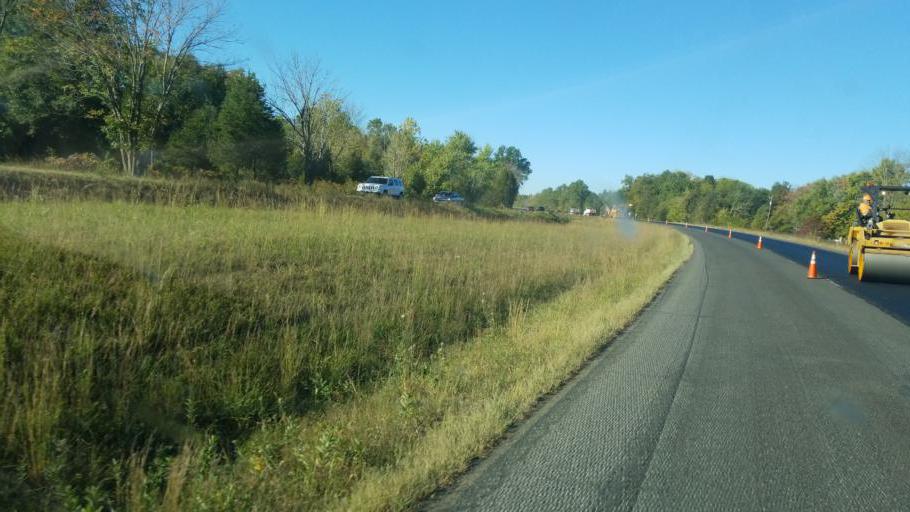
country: US
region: Virginia
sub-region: Fauquier County
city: Bealeton
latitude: 38.5236
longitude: -77.8308
